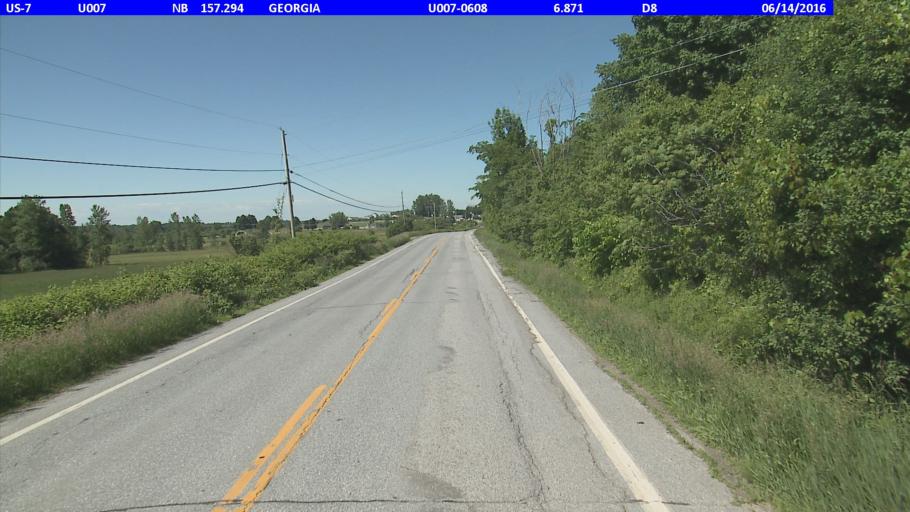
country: US
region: Vermont
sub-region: Franklin County
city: Saint Albans
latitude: 44.7700
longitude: -73.1079
